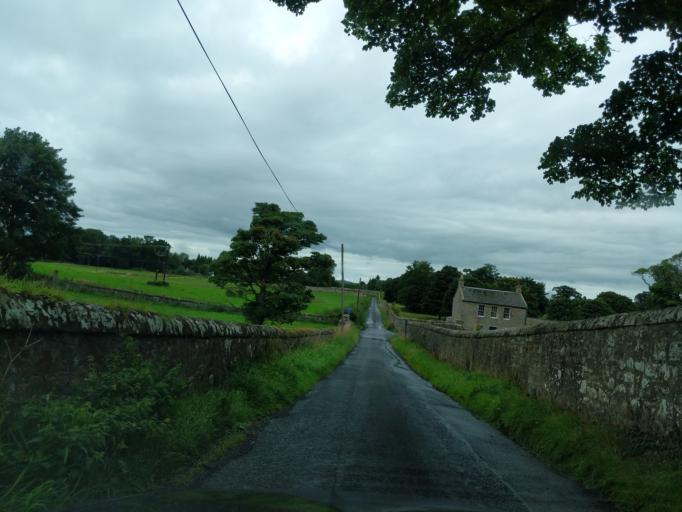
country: GB
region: Scotland
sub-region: Fife
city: Limekilns
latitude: 55.9910
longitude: -3.4722
